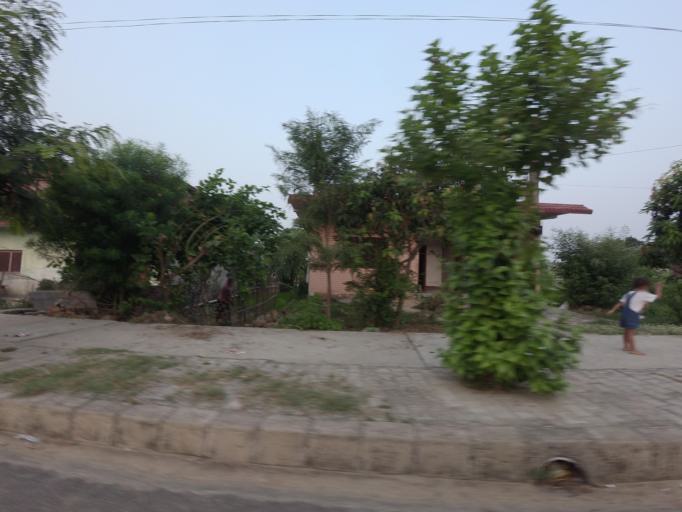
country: NP
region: Western Region
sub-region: Lumbini Zone
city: Bhairahawa
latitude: 27.5019
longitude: 83.4636
